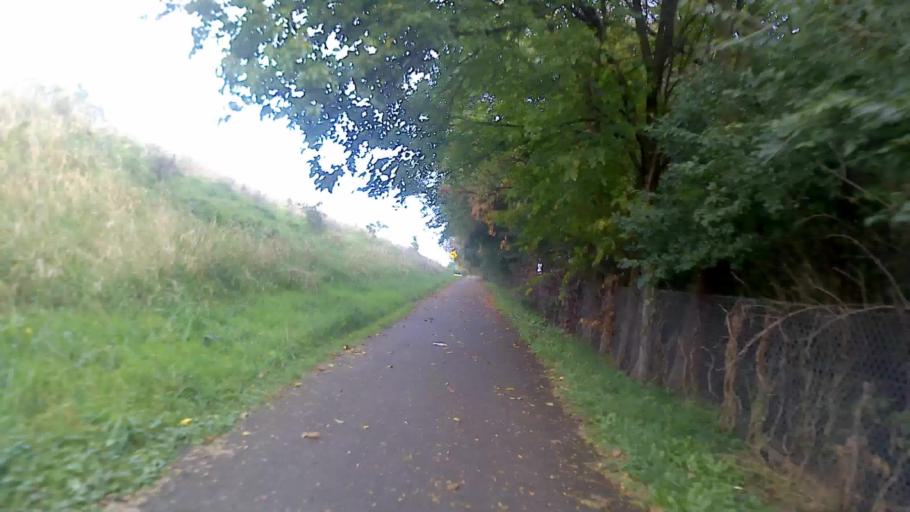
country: US
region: Illinois
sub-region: DuPage County
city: Warrenville
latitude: 41.8299
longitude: -88.1620
